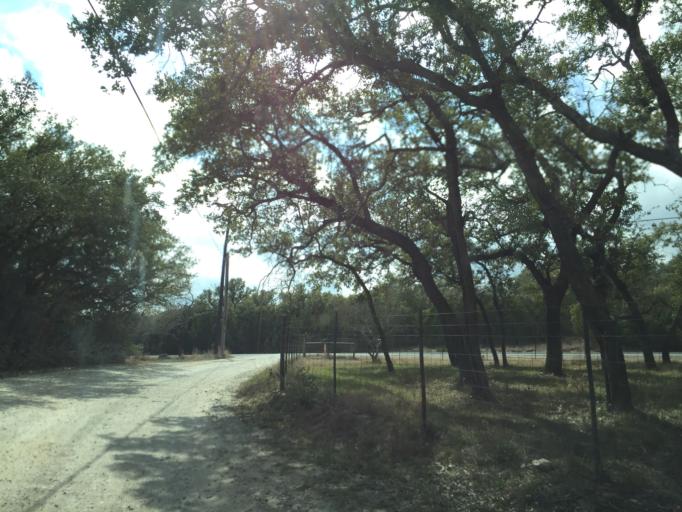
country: US
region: Texas
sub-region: Travis County
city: Briarcliff
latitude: 30.3824
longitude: -98.0955
